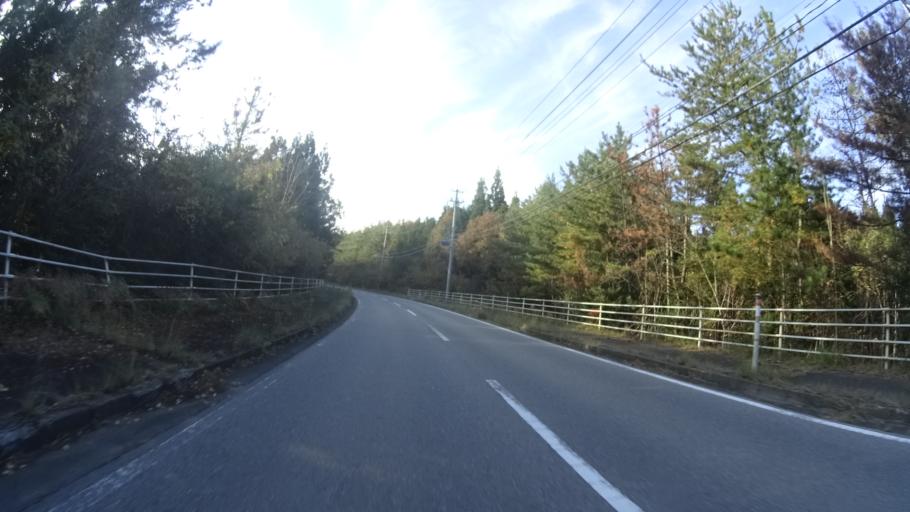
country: JP
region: Ishikawa
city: Hakui
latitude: 37.0668
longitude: 136.7652
